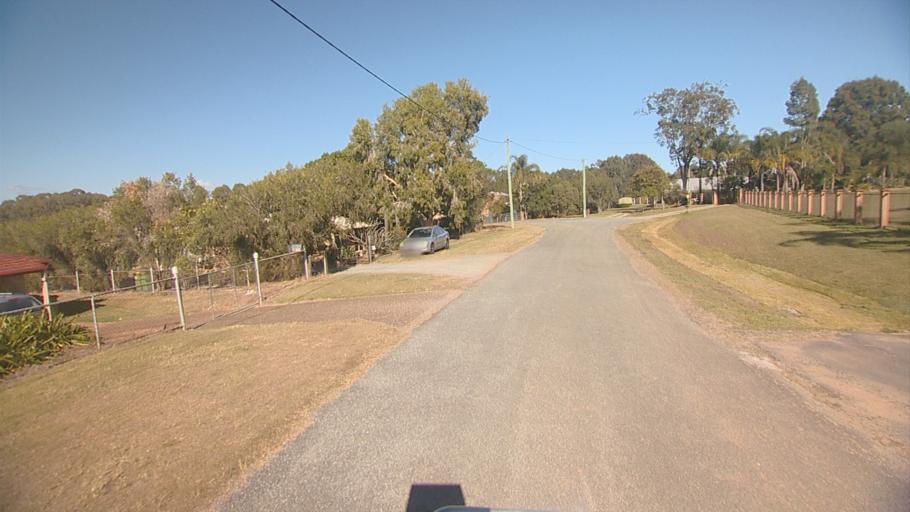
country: AU
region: Queensland
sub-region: Logan
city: Chambers Flat
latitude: -27.7616
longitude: 153.0944
